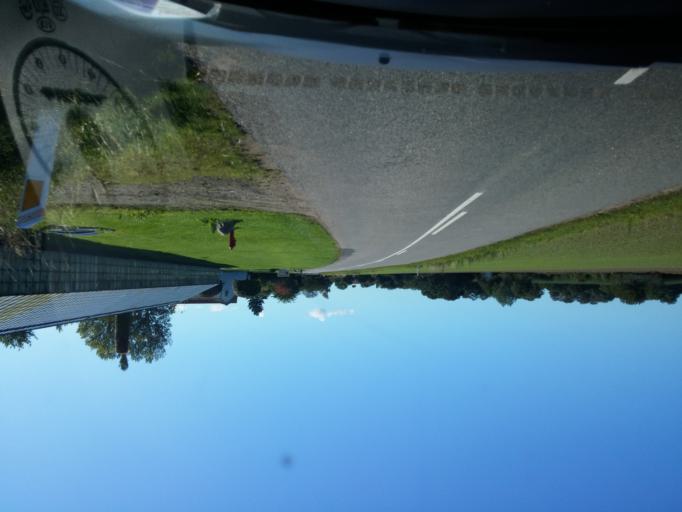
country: DK
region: South Denmark
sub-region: Kerteminde Kommune
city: Munkebo
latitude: 55.4056
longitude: 10.5498
